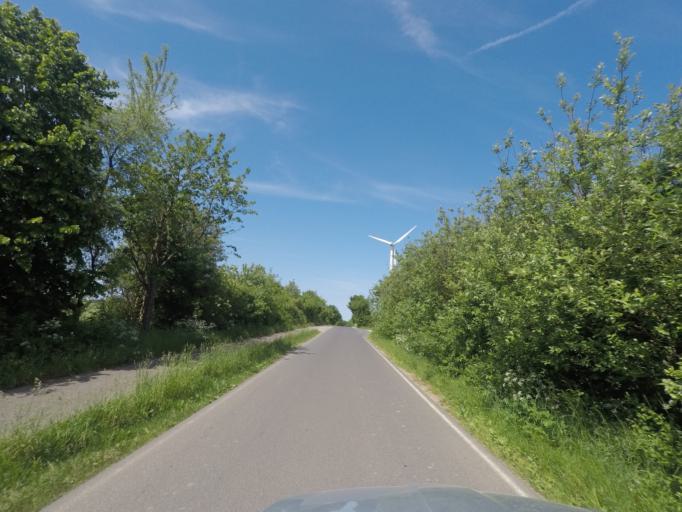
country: DE
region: Brandenburg
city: Britz
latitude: 52.8749
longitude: 13.7640
